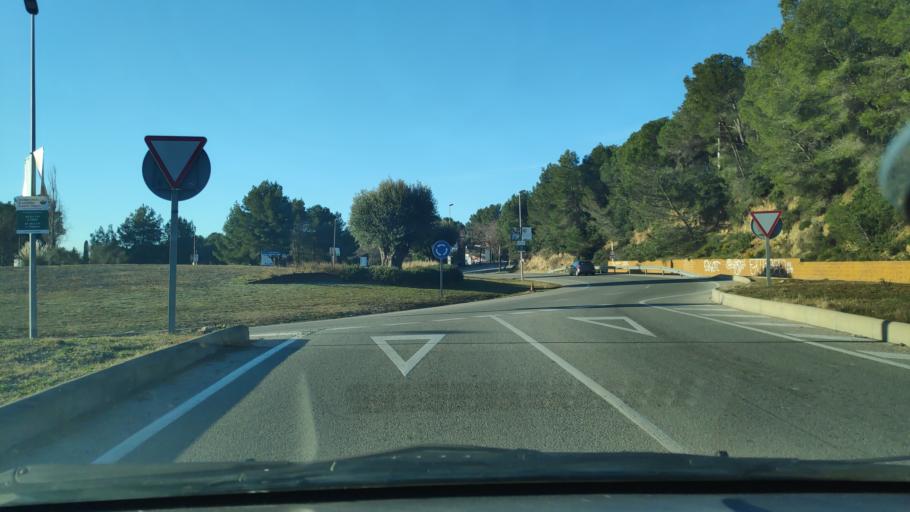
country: ES
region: Catalonia
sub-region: Provincia de Barcelona
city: Sant Quirze del Valles
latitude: 41.5098
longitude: 2.0920
